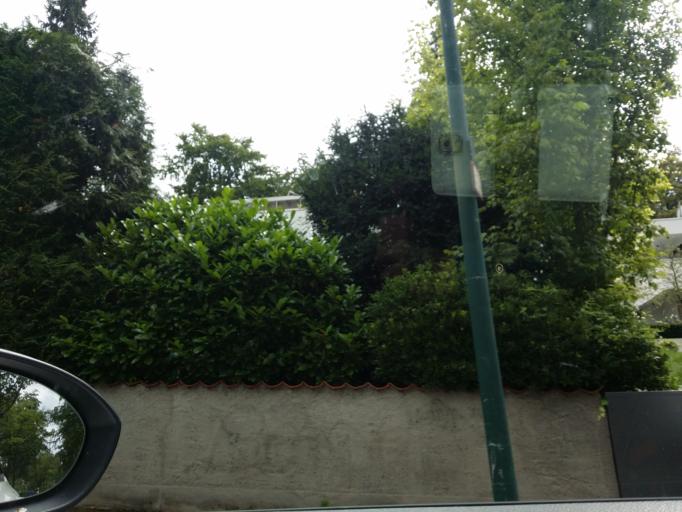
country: DE
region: Hesse
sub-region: Regierungsbezirk Darmstadt
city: Darmstadt
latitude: 49.8398
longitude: 8.6500
